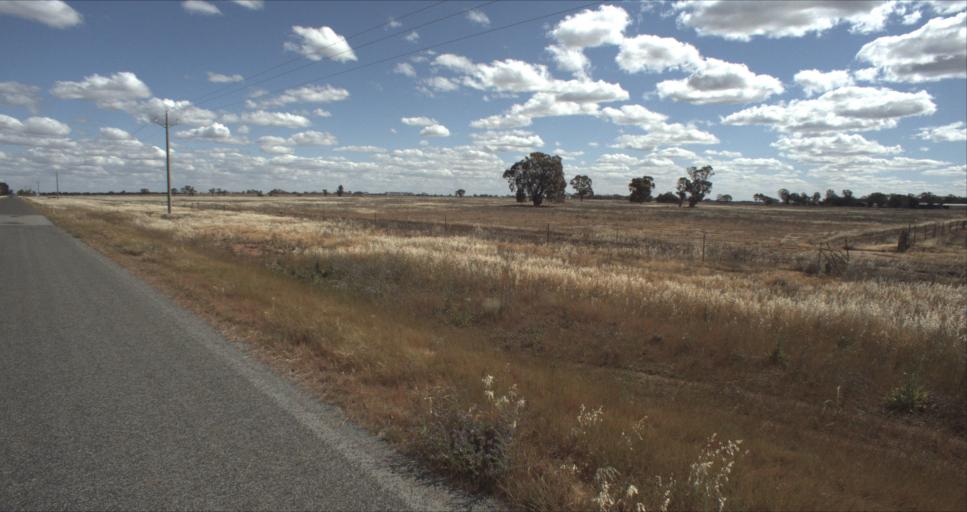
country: AU
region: New South Wales
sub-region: Leeton
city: Leeton
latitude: -34.4648
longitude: 146.2520
